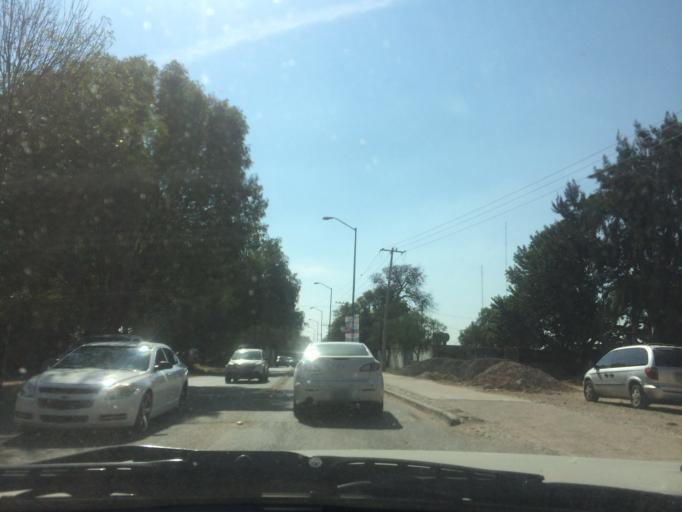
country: MX
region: Guanajuato
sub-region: Leon
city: Medina
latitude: 21.1760
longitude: -101.6540
